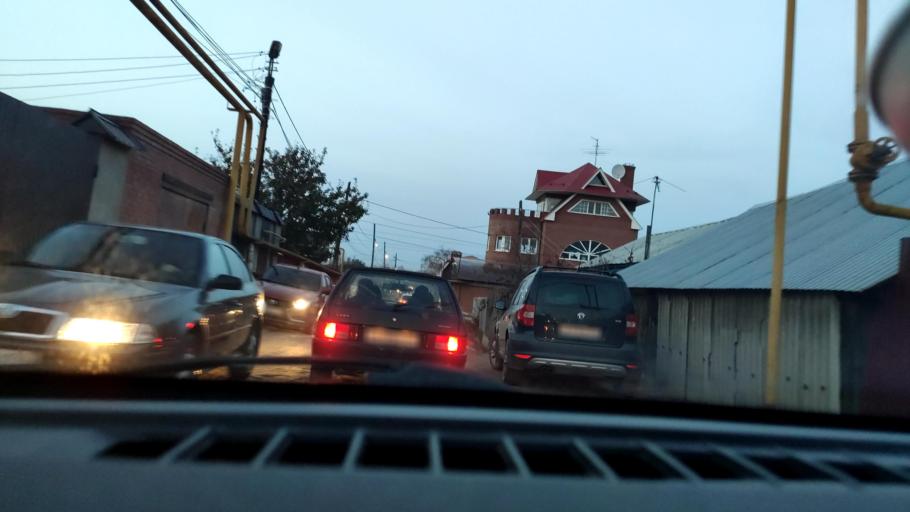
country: RU
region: Samara
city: Samara
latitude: 53.1357
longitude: 50.0954
